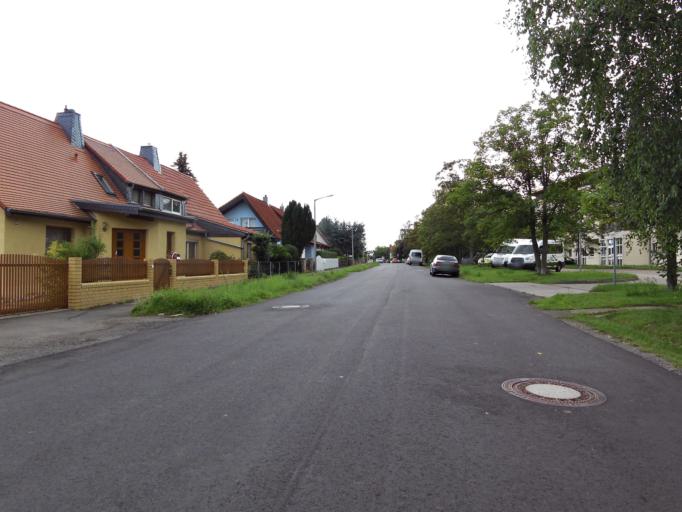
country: DE
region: Saxony
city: Leipzig
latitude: 51.3818
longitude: 12.4070
